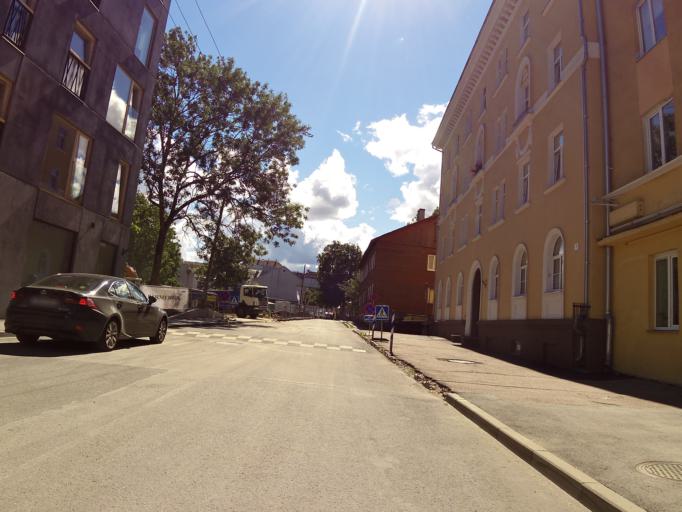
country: EE
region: Harju
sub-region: Tallinna linn
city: Tallinn
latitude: 59.4426
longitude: 24.7382
